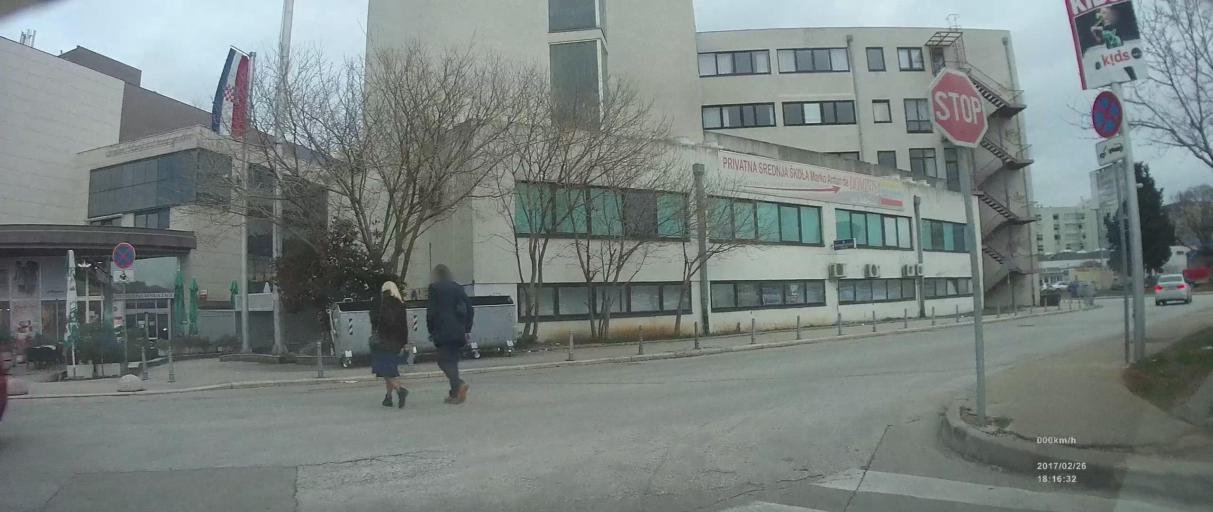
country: HR
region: Splitsko-Dalmatinska
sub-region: Grad Split
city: Split
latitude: 43.5197
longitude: 16.4455
